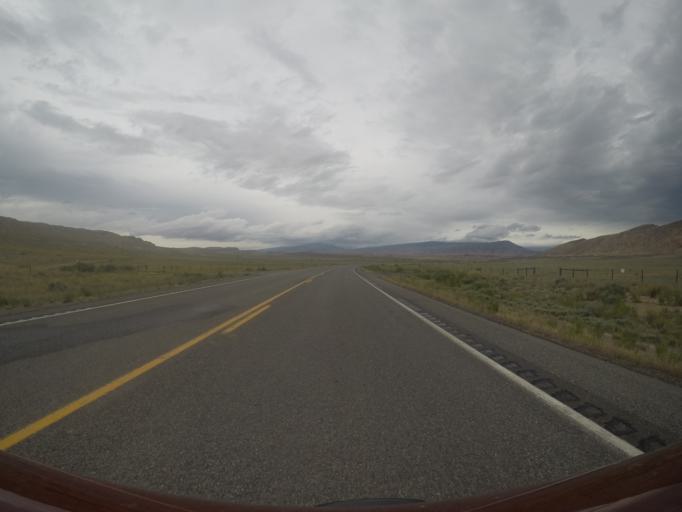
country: US
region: Wyoming
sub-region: Big Horn County
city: Lovell
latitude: 44.9239
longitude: -108.2986
